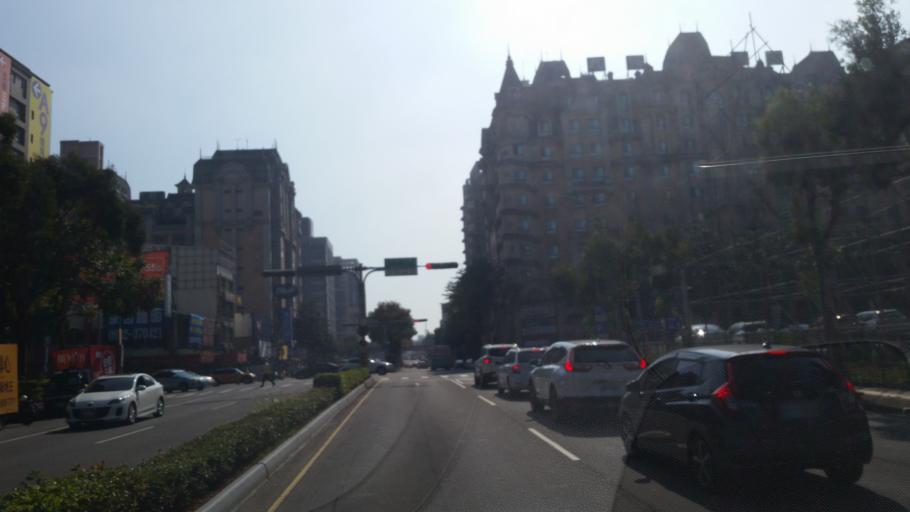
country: TW
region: Taiwan
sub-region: Taoyuan
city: Taoyuan
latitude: 25.0722
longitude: 121.3683
